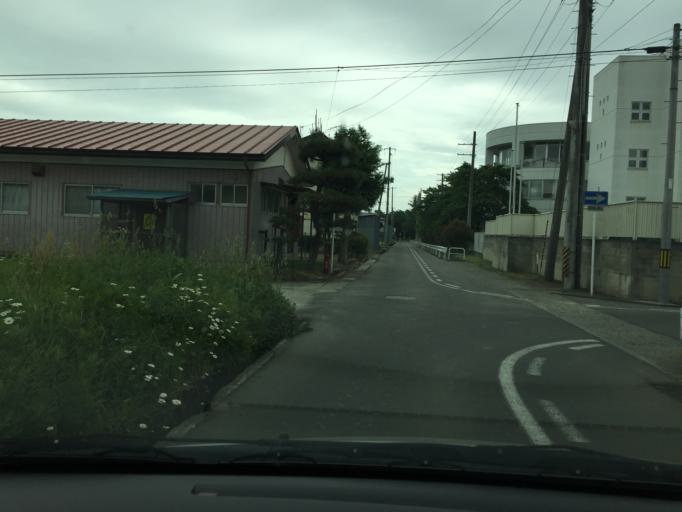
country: JP
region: Fukushima
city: Kitakata
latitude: 37.6682
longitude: 139.8745
